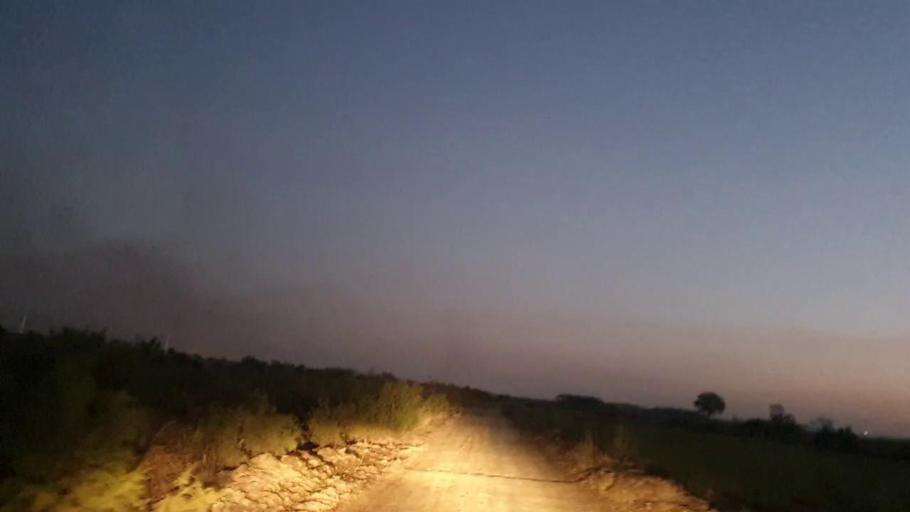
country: PK
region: Sindh
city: Nawabshah
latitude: 26.3262
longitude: 68.3770
